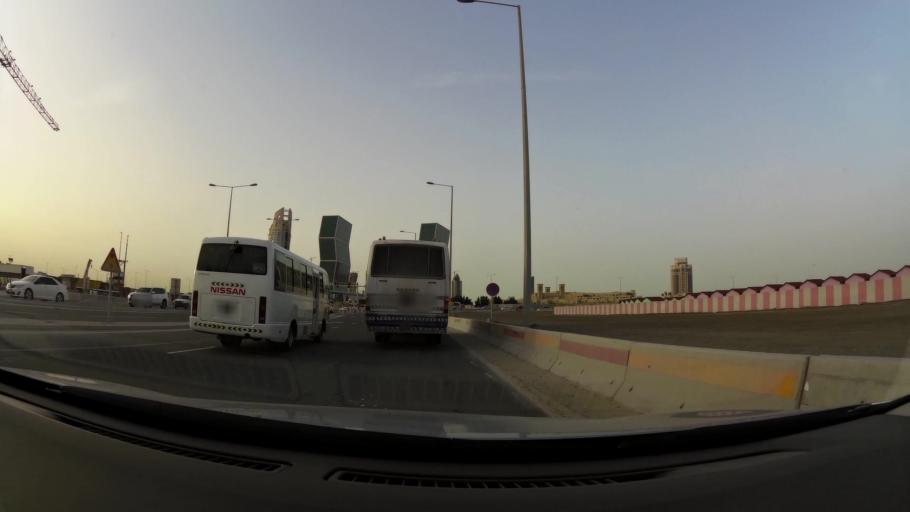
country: QA
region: Baladiyat ad Dawhah
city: Doha
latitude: 25.3714
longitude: 51.5256
